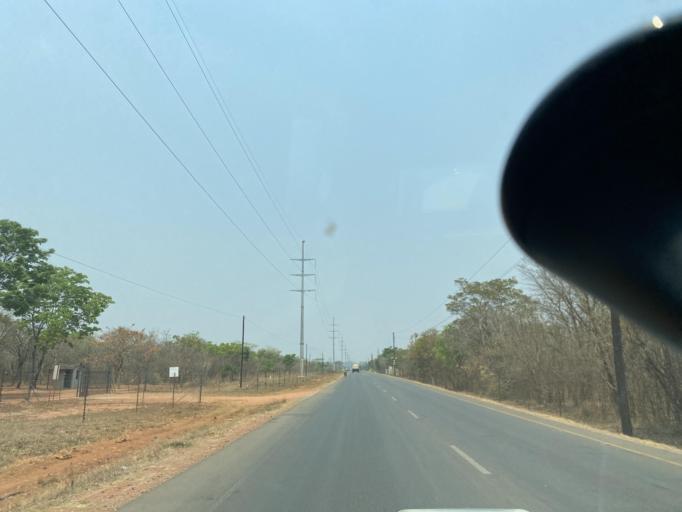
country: ZM
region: Lusaka
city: Lusaka
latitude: -15.5105
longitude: 28.4491
